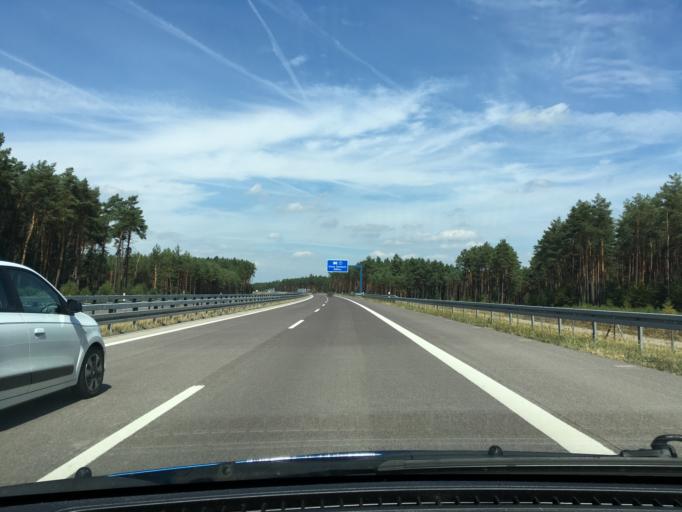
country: DE
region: Mecklenburg-Vorpommern
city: Gross Laasch
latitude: 53.3977
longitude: 11.5327
